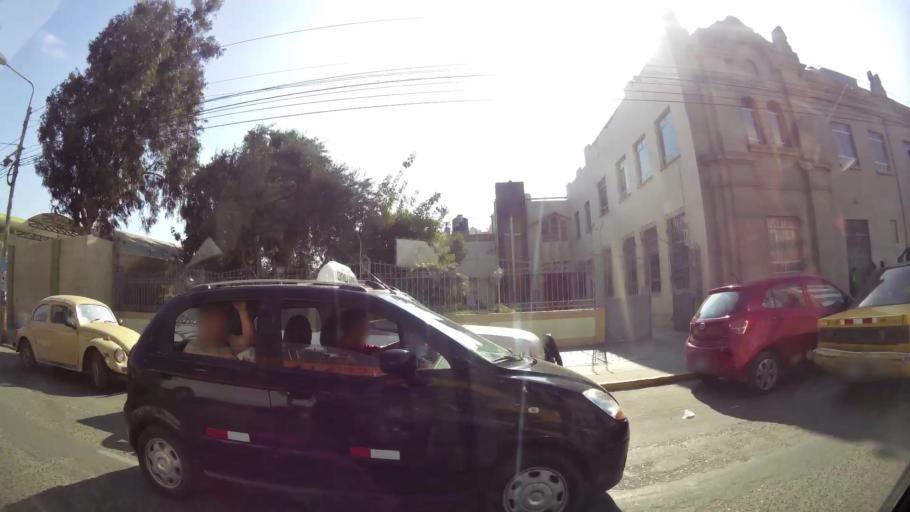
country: PE
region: Lambayeque
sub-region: Provincia de Chiclayo
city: Chiclayo
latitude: -6.7659
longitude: -79.8417
